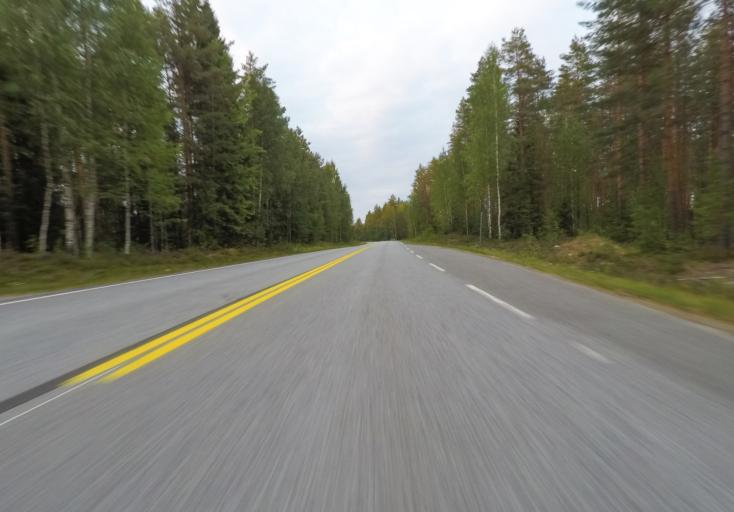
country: FI
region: Central Finland
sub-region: Jyvaeskylae
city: Toivakka
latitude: 62.1766
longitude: 26.1765
